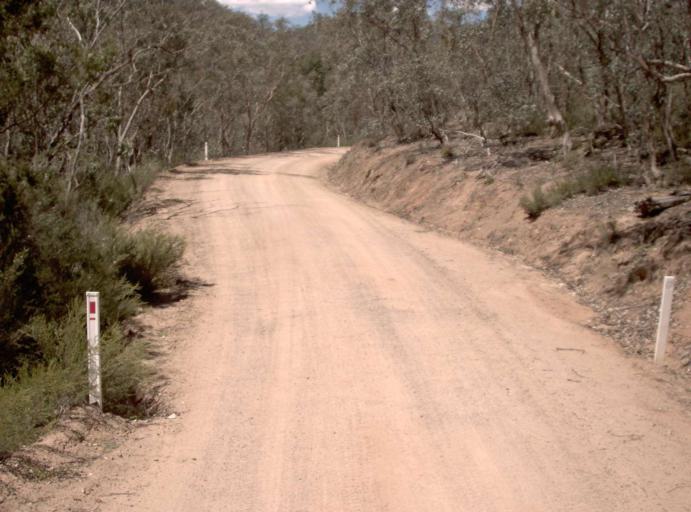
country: AU
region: New South Wales
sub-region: Snowy River
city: Jindabyne
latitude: -37.0620
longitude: 148.5182
